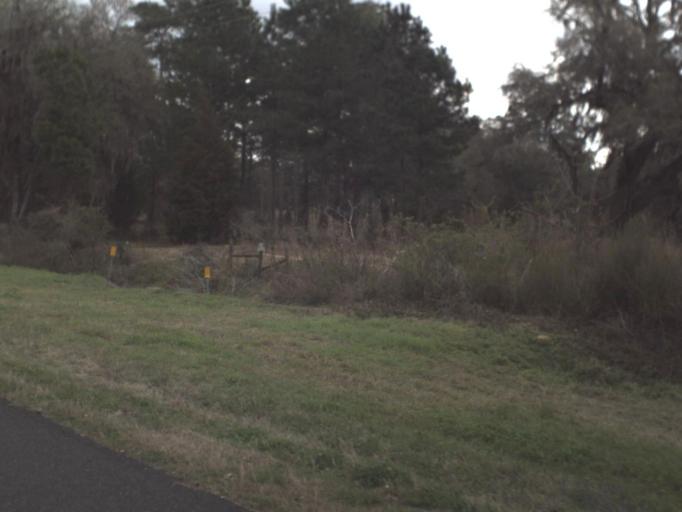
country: US
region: Florida
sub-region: Leon County
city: Tallahassee
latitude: 30.6122
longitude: -84.1744
